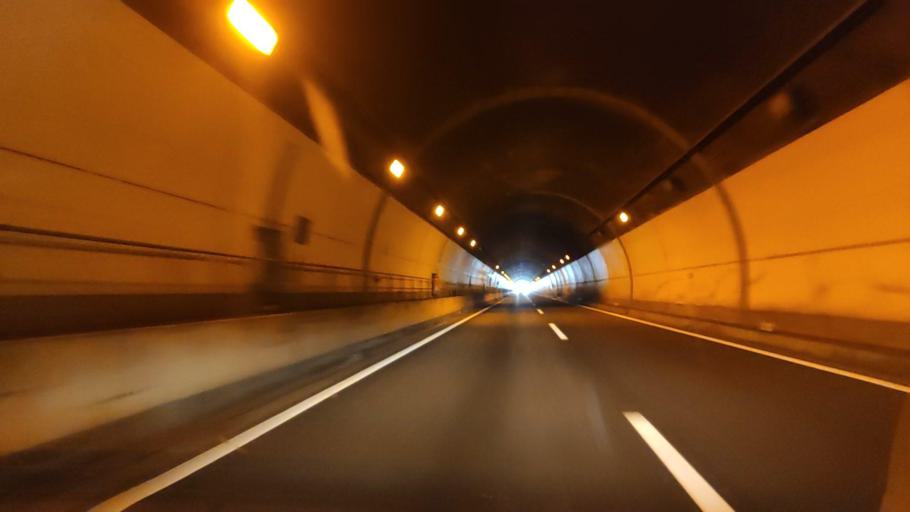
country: JP
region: Akita
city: Hanawa
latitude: 40.0147
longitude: 140.9866
